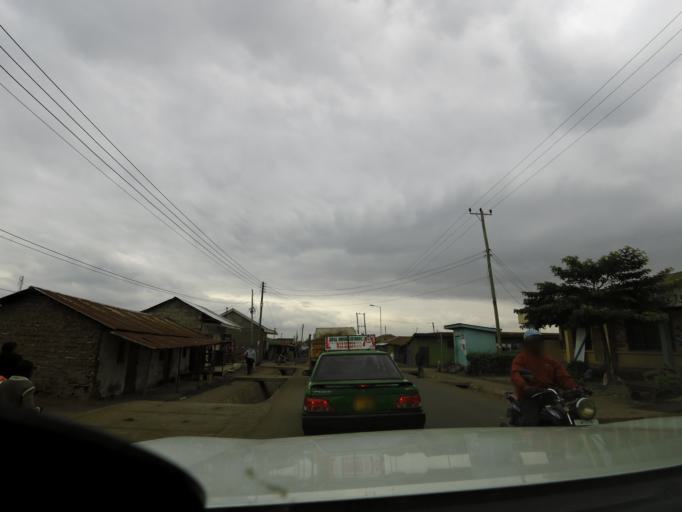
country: TZ
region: Arusha
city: Arusha
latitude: -3.3712
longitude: 36.6607
